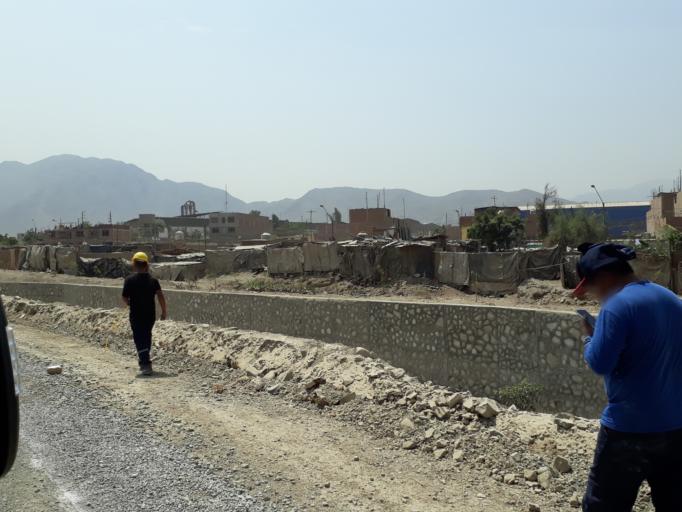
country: PE
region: Lima
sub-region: Lima
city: Santa Maria
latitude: -11.9969
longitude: -76.9140
